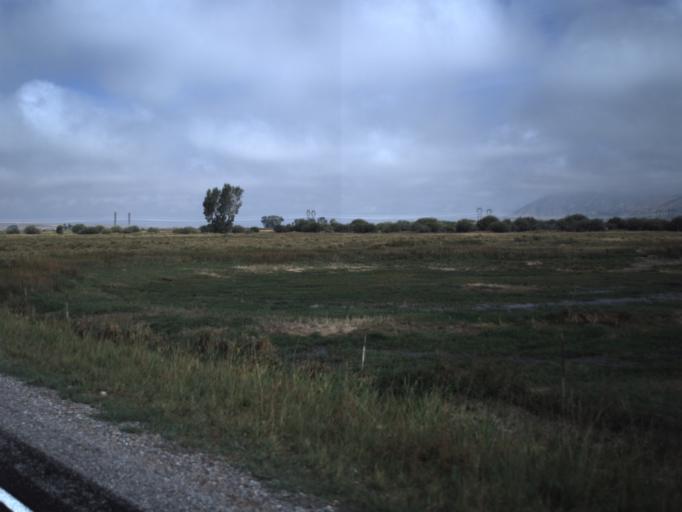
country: US
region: Utah
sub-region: Rich County
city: Randolph
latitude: 41.5148
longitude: -111.1361
